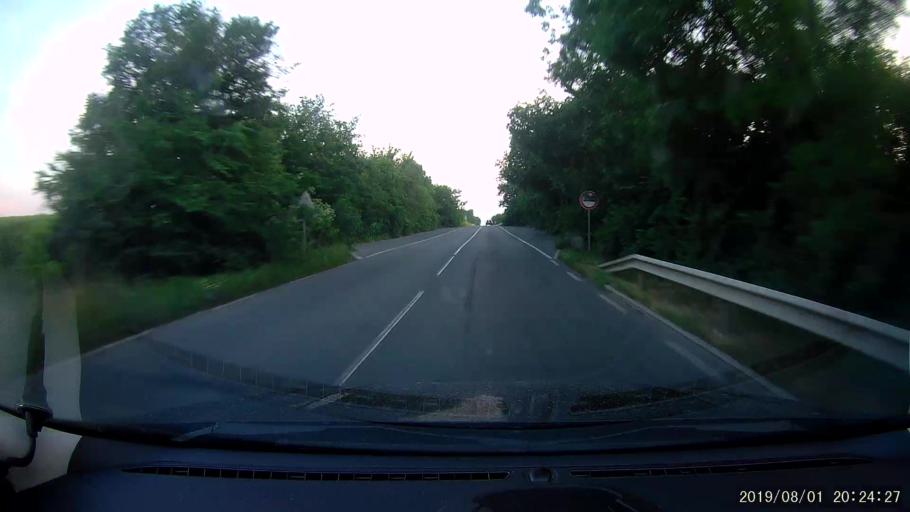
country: BG
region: Yambol
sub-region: Obshtina Elkhovo
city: Elkhovo
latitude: 42.2314
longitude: 26.5935
